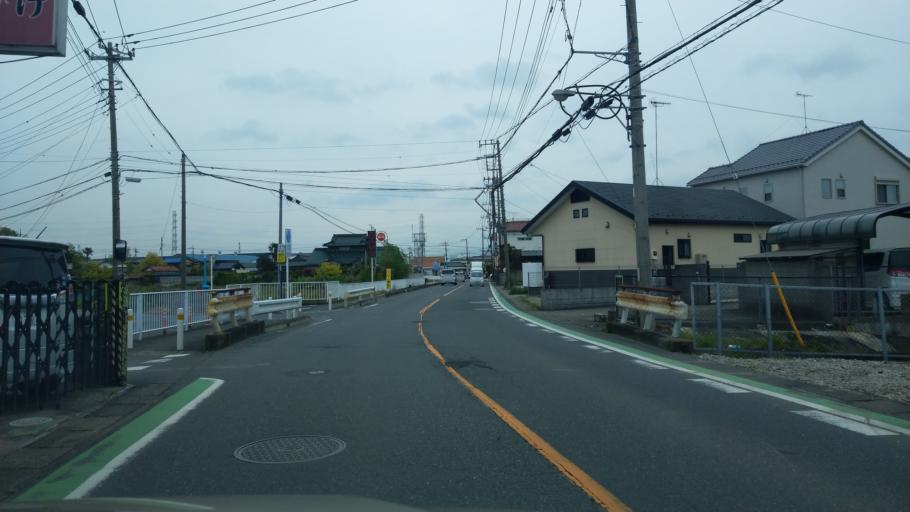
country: JP
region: Saitama
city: Kasukabe
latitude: 35.9478
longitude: 139.7252
